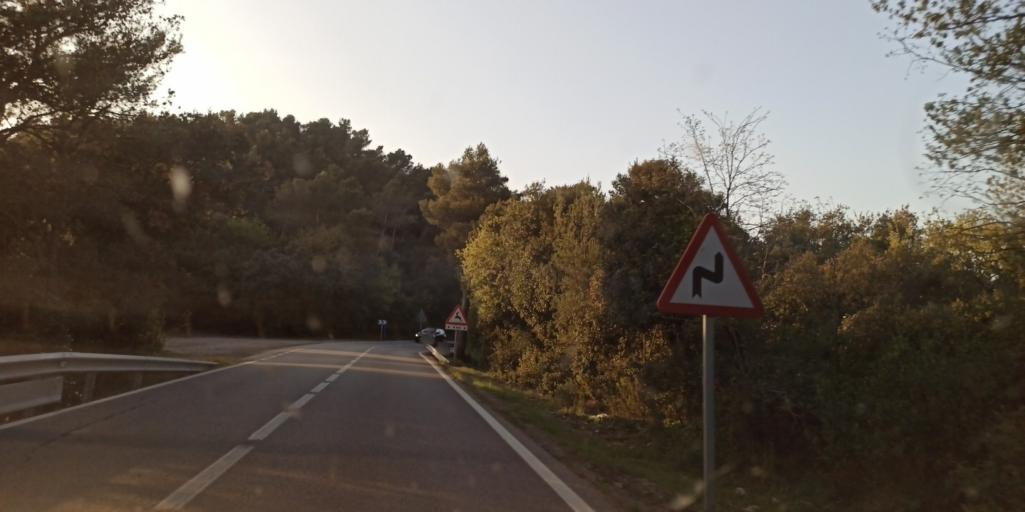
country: ES
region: Catalonia
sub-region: Provincia de Barcelona
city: Sant Cugat del Valles
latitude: 41.4362
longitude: 2.1058
